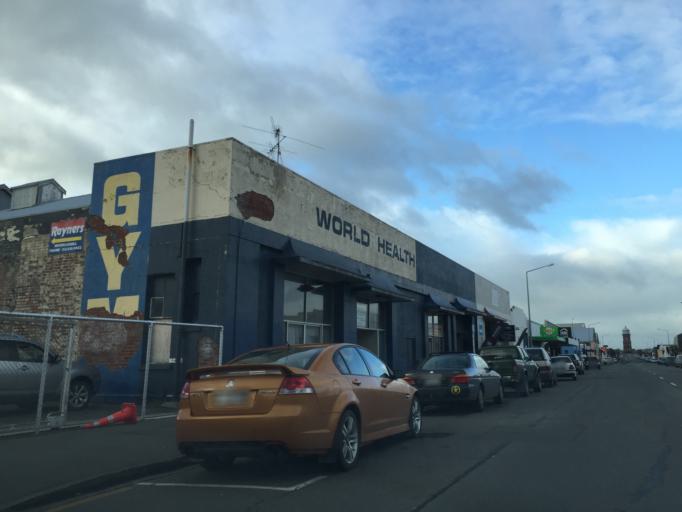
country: NZ
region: Southland
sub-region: Invercargill City
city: Invercargill
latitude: -46.4075
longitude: 168.3482
